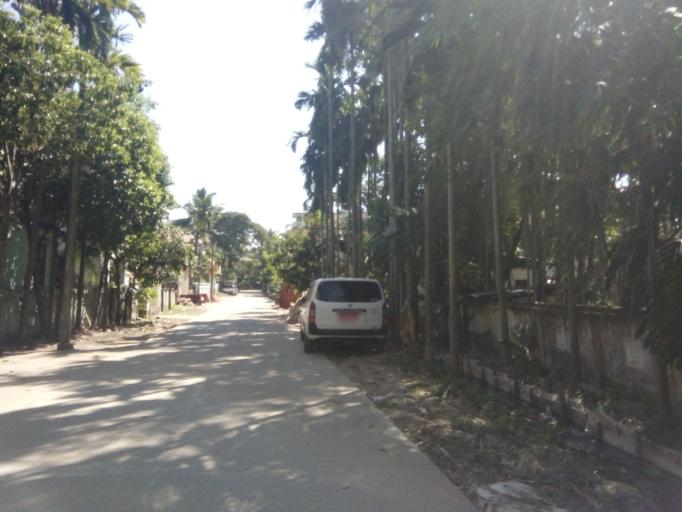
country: MM
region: Yangon
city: Yangon
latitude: 16.9206
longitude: 96.1596
